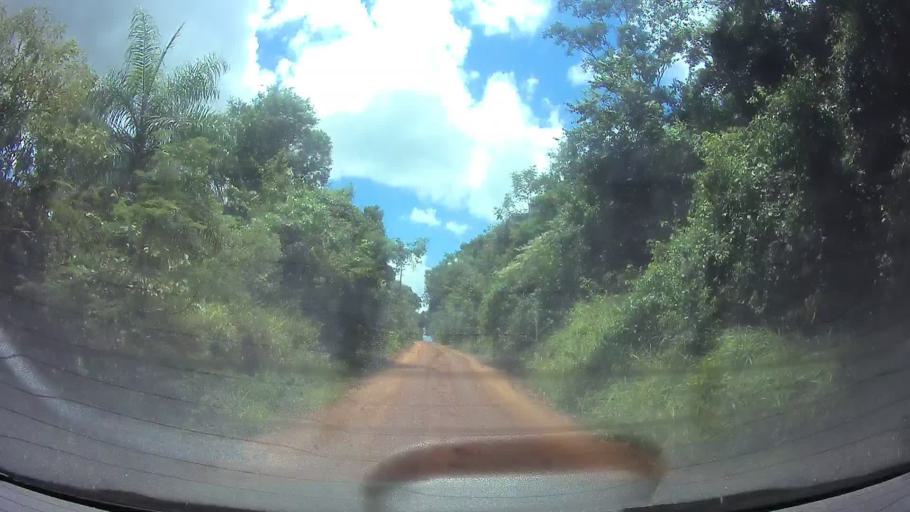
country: PY
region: Paraguari
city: La Colmena
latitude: -25.9478
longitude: -56.7816
